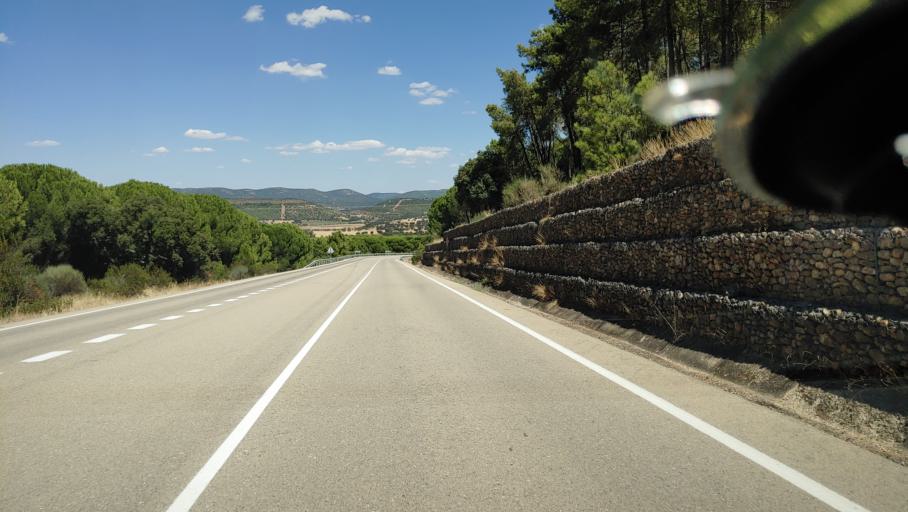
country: ES
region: Castille-La Mancha
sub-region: Provincia de Ciudad Real
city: Saceruela
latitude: 39.0081
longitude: -4.5062
